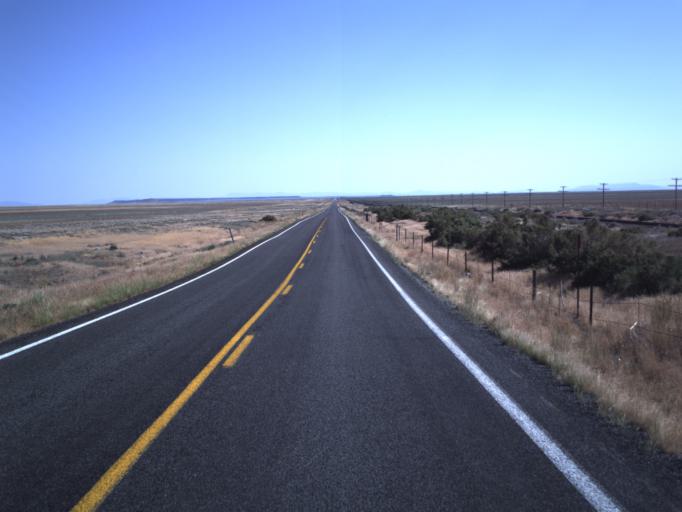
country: US
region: Utah
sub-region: Millard County
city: Delta
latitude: 38.9891
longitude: -112.7919
